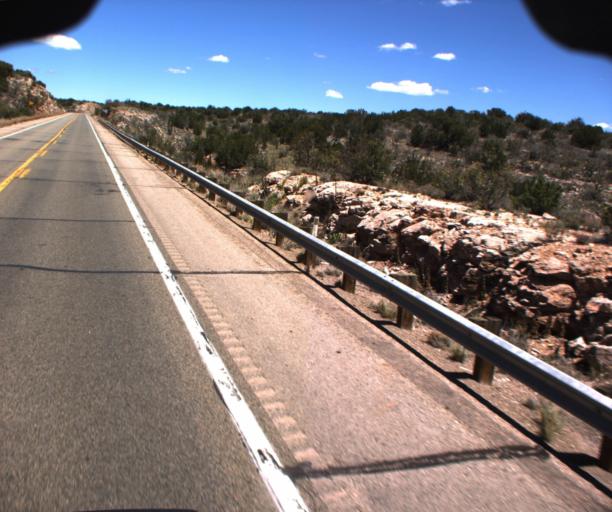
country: US
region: Arizona
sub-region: Yavapai County
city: Paulden
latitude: 34.9277
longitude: -112.4456
